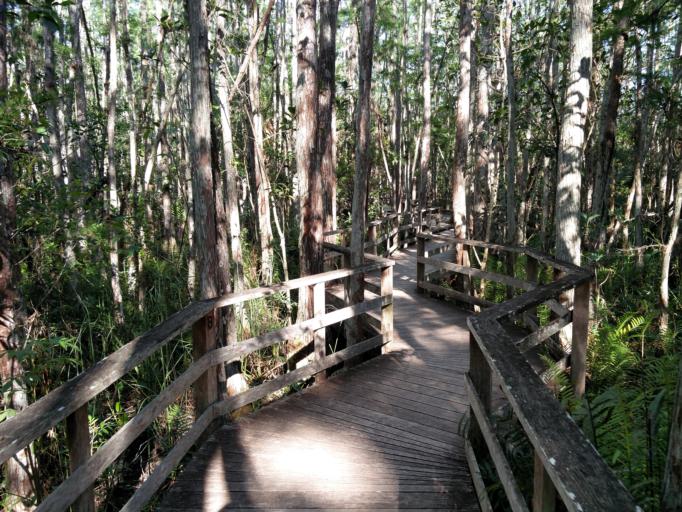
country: US
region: Florida
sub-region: Collier County
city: Orangetree
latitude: 26.3770
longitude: -81.6072
